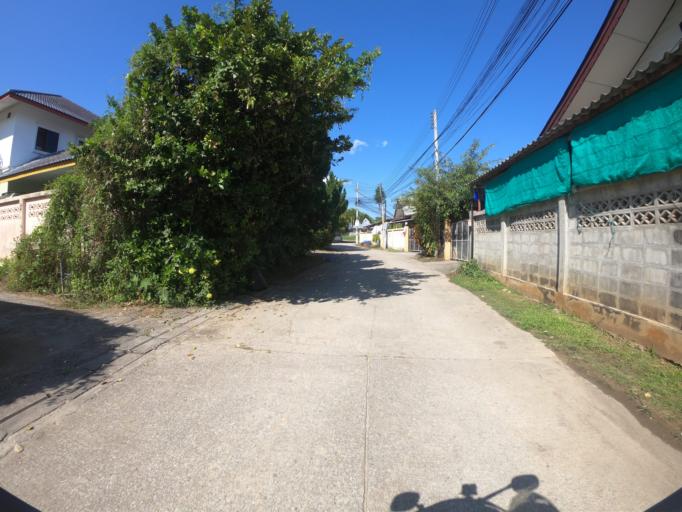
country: TH
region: Chiang Mai
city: Chiang Mai
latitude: 18.7627
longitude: 98.9477
